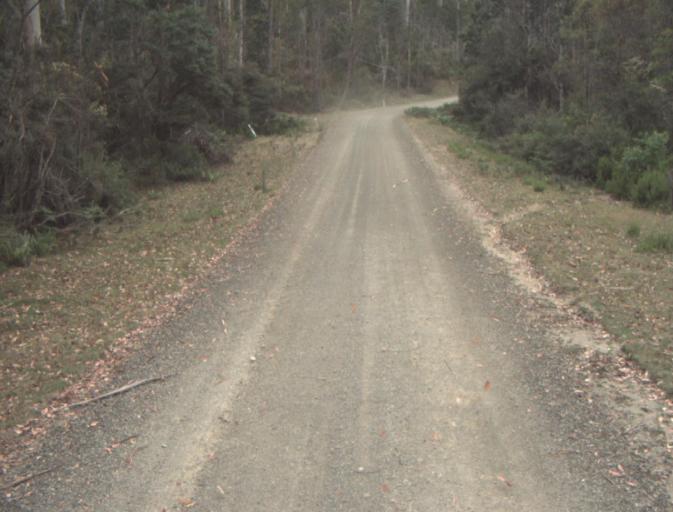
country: AU
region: Tasmania
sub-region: Dorset
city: Scottsdale
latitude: -41.4095
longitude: 147.5171
